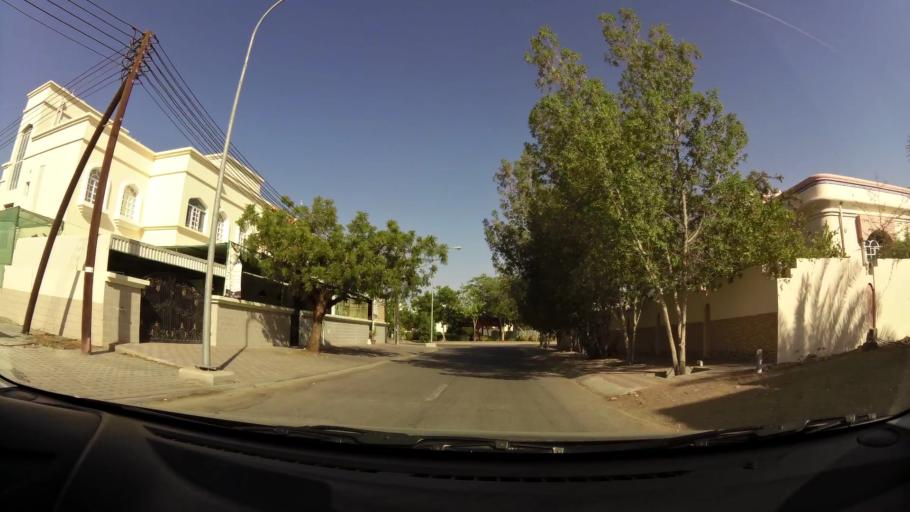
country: OM
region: Muhafazat Masqat
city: As Sib al Jadidah
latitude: 23.6167
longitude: 58.2112
